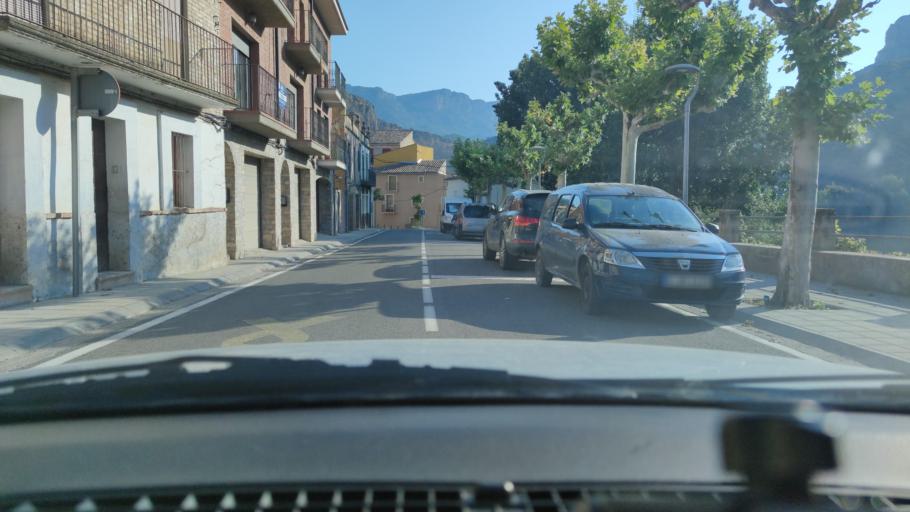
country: ES
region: Catalonia
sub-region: Provincia de Lleida
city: Camarasa
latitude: 41.8680
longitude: 0.8413
